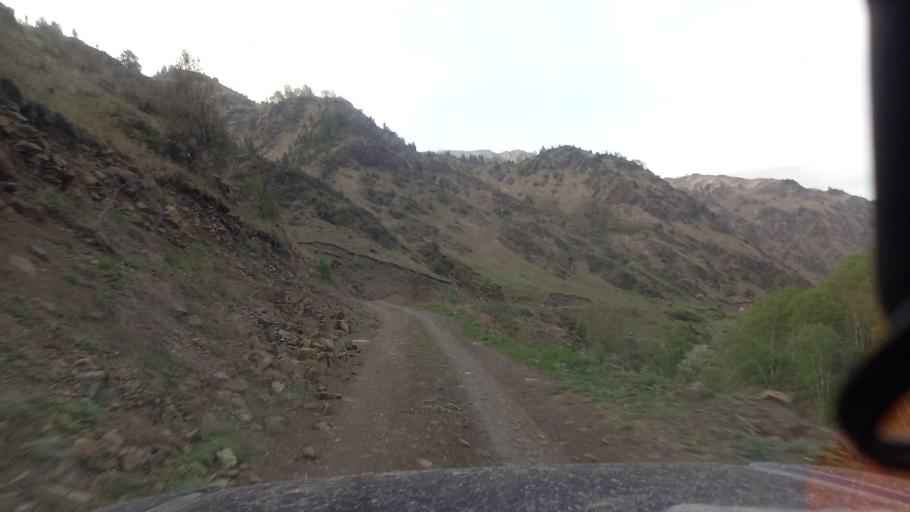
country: RU
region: Kabardino-Balkariya
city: Kamennomostskoye
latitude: 43.7209
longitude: 42.8445
